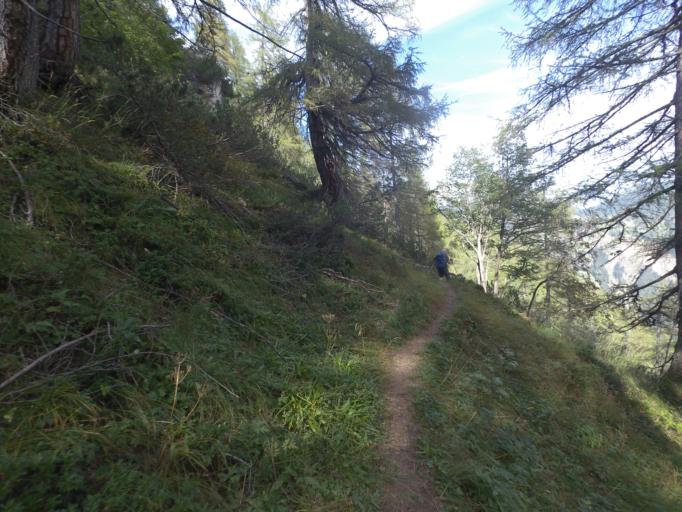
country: AT
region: Salzburg
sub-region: Politischer Bezirk Sankt Johann im Pongau
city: Kleinarl
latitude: 47.2410
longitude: 13.4116
